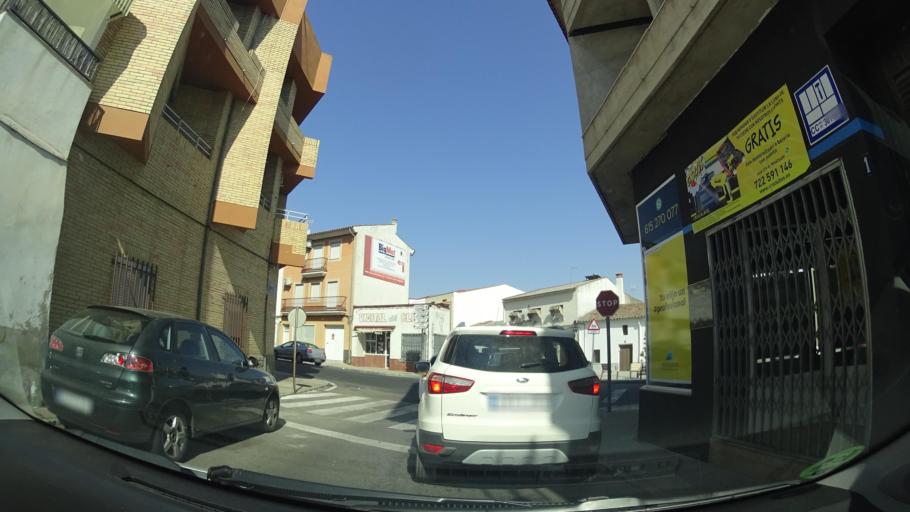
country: ES
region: Extremadura
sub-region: Provincia de Caceres
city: Miajadas
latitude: 39.1481
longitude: -5.9127
